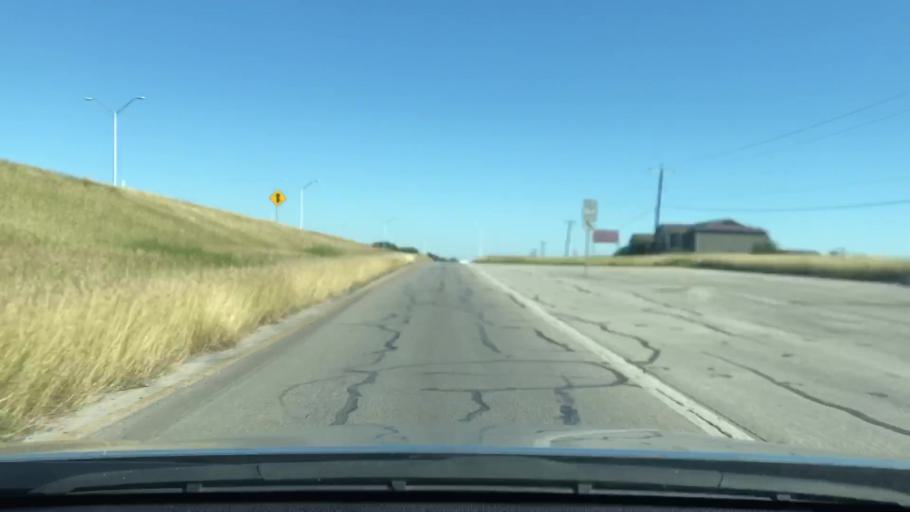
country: US
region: Texas
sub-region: Bexar County
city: Universal City
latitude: 29.5449
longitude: -98.3134
